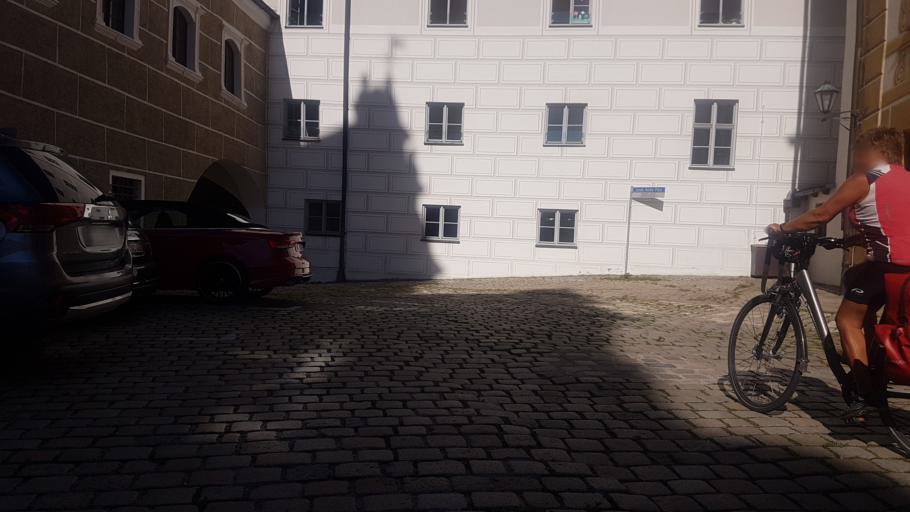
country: DE
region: Bavaria
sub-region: Upper Bavaria
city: Neuburg an der Donau
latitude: 48.7376
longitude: 11.1805
